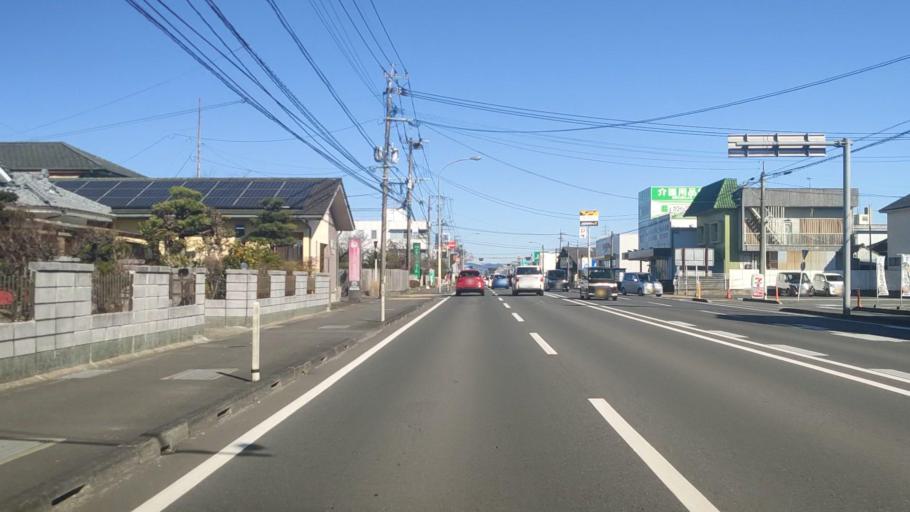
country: JP
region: Miyazaki
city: Miyakonojo
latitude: 31.7427
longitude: 131.0740
